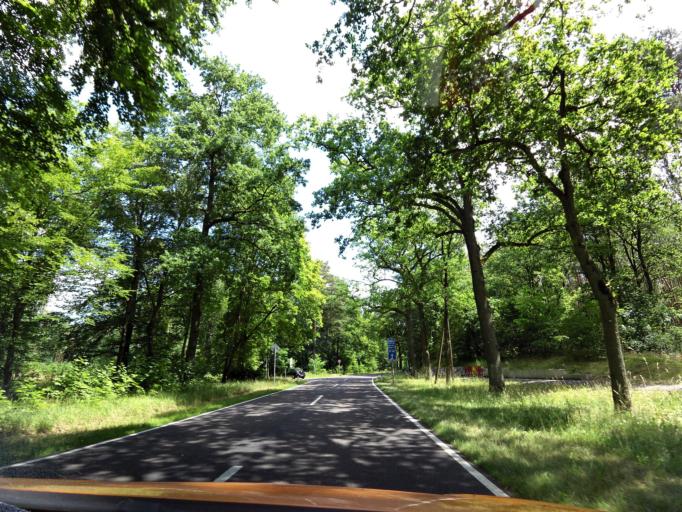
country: DE
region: Brandenburg
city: Nauen
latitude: 52.6293
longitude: 12.9296
